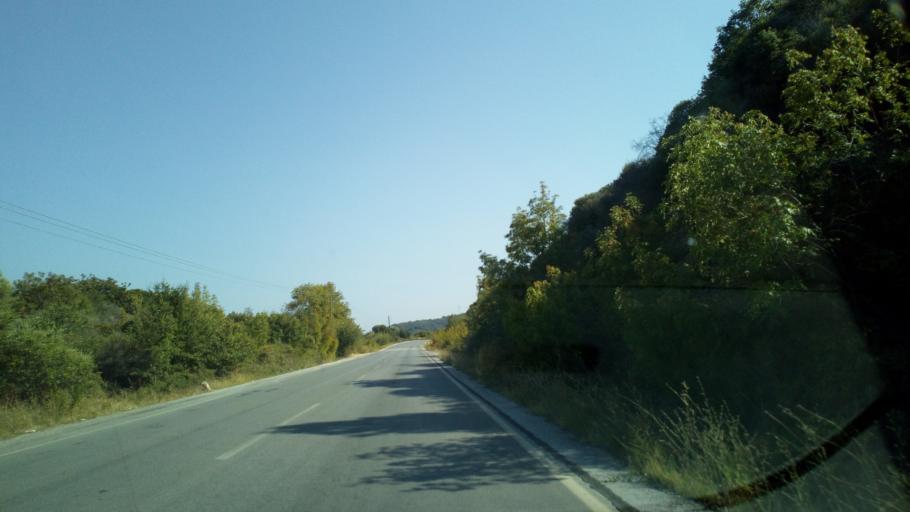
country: GR
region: Central Macedonia
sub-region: Nomos Thessalonikis
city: Stavros
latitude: 40.6459
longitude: 23.7458
